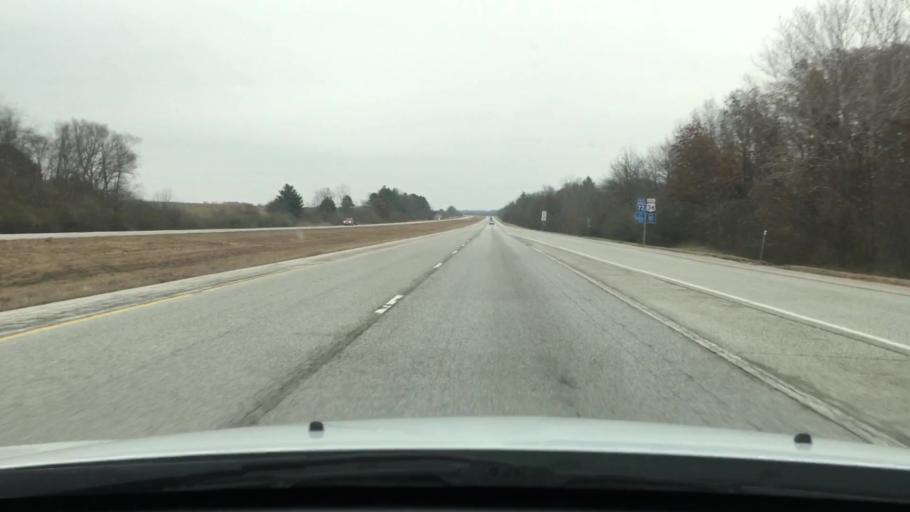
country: US
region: Illinois
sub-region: Morgan County
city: South Jacksonville
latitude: 39.6802
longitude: -90.2888
